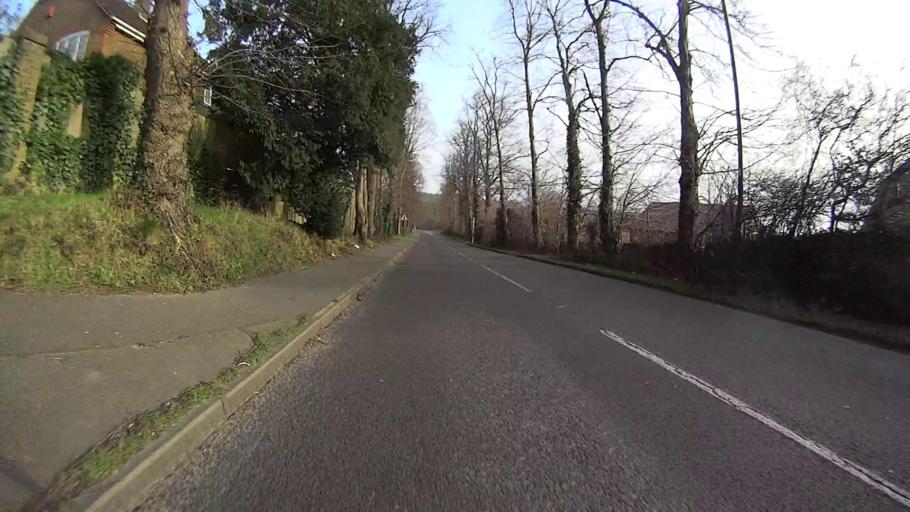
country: GB
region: England
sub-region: West Sussex
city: Maidenbower
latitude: 51.1104
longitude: -0.1461
